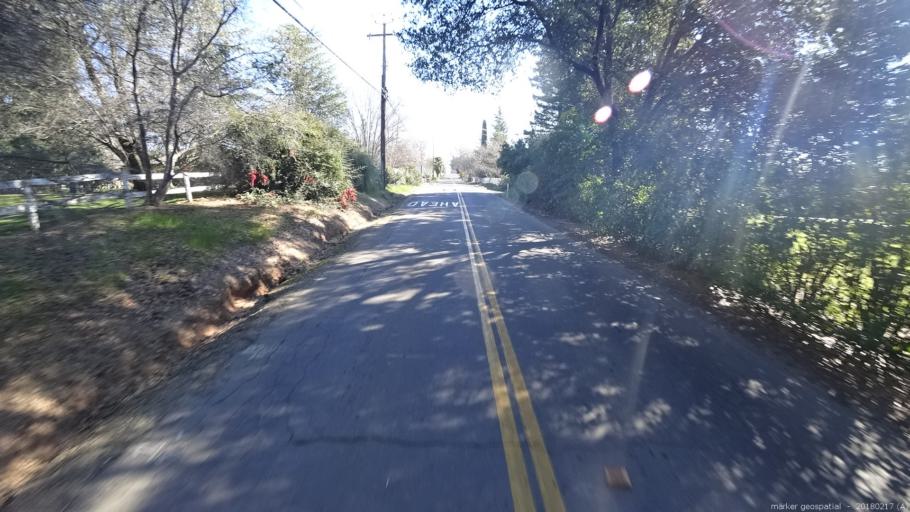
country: US
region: California
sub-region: Sacramento County
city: Orangevale
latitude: 38.7111
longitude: -121.2195
